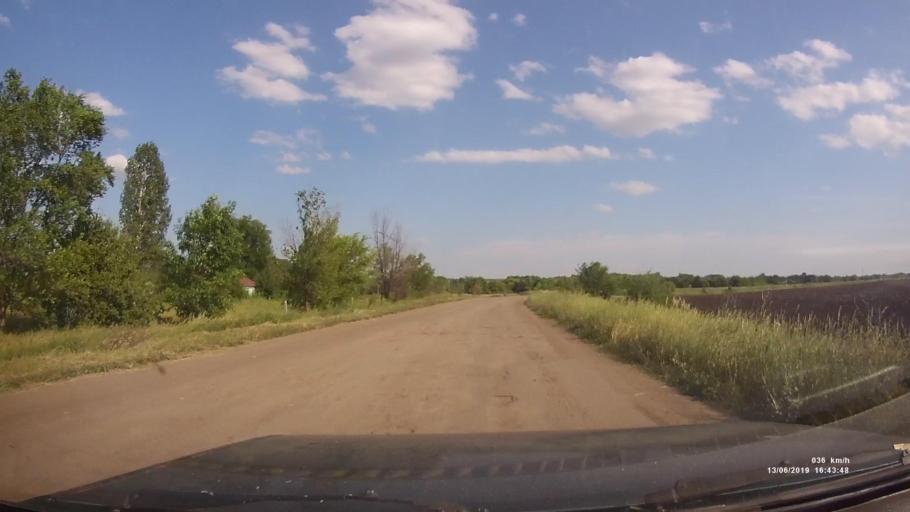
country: RU
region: Rostov
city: Kazanskaya
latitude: 49.9486
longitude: 41.4215
